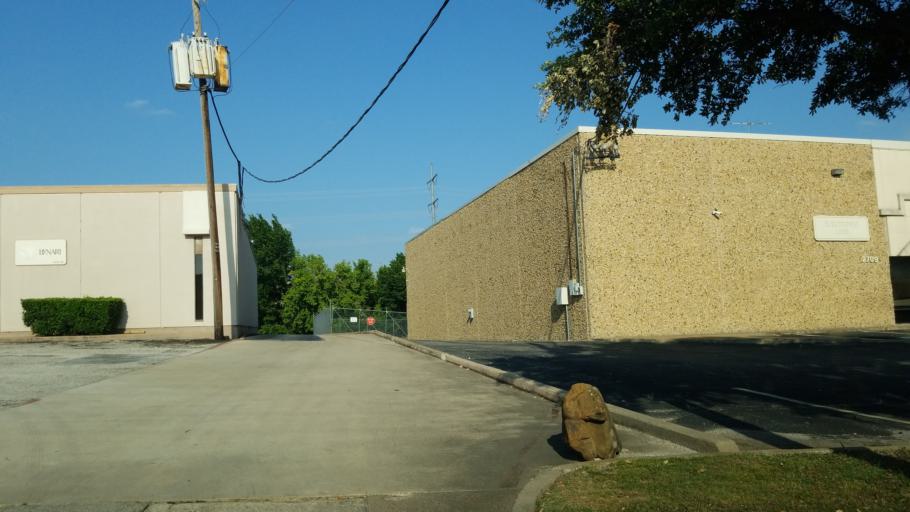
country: US
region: Texas
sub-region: Dallas County
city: Farmers Branch
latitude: 32.8762
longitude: -96.8932
